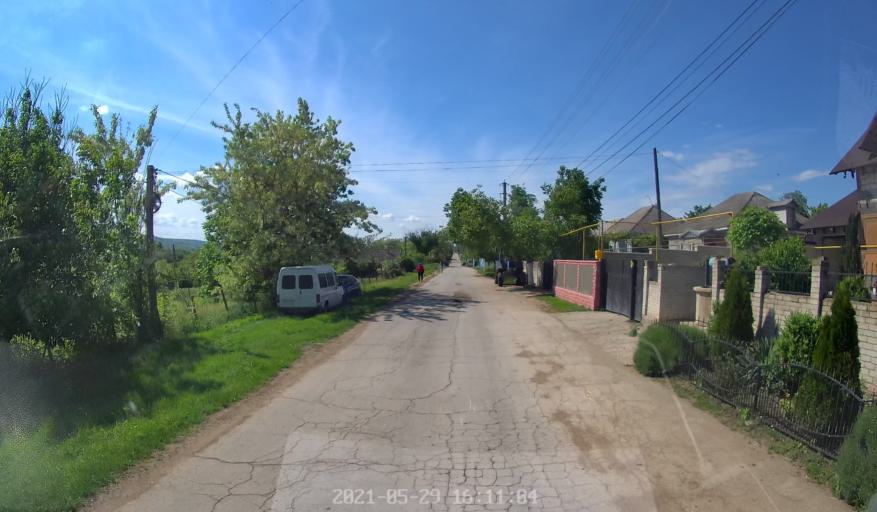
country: MD
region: Chisinau
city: Singera
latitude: 46.8245
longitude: 28.8787
